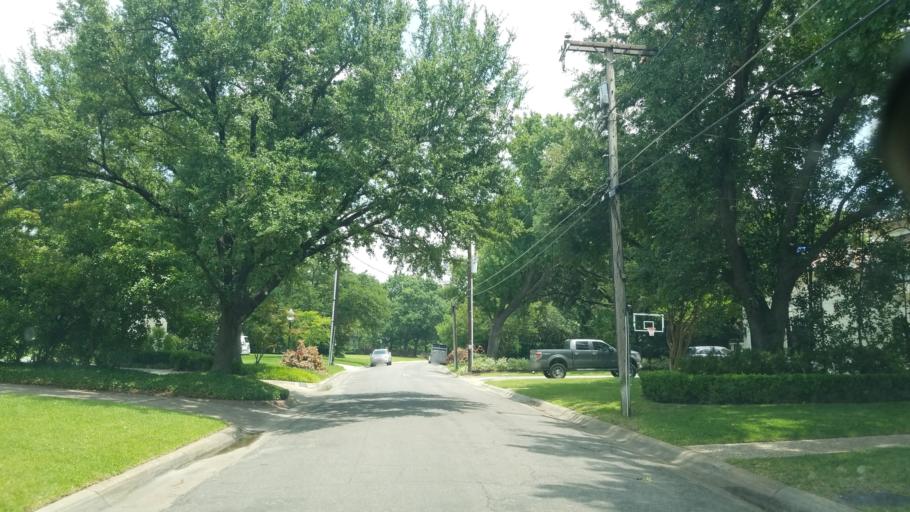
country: US
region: Texas
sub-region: Dallas County
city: University Park
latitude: 32.8403
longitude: -96.8171
